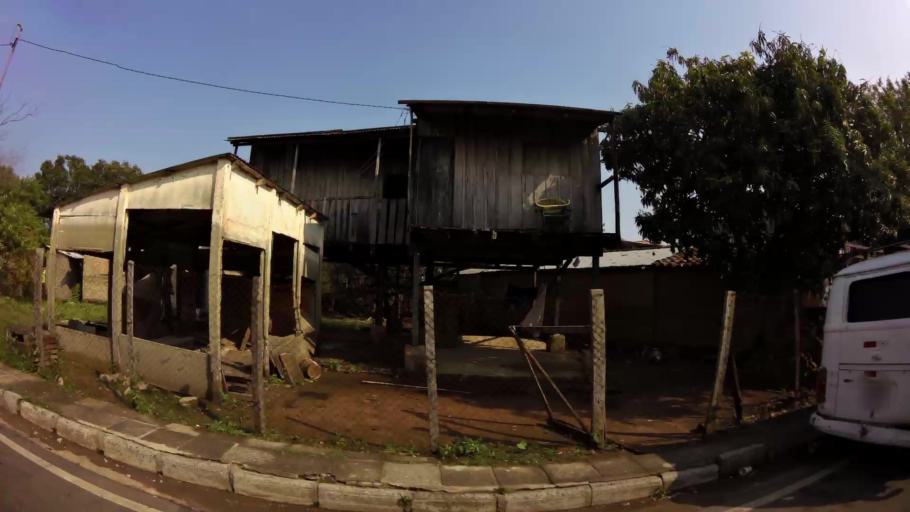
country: PY
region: Asuncion
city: Asuncion
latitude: -25.3151
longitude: -57.6697
